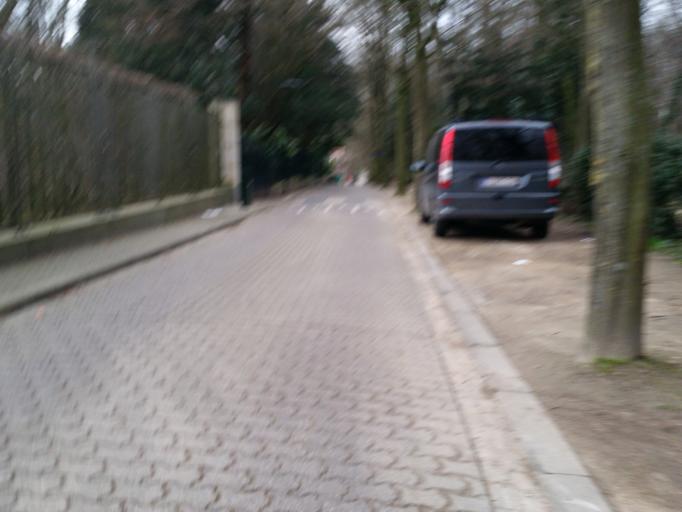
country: BE
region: Flanders
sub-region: Provincie Vlaams-Brabant
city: Linkebeek
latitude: 50.8014
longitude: 4.3781
